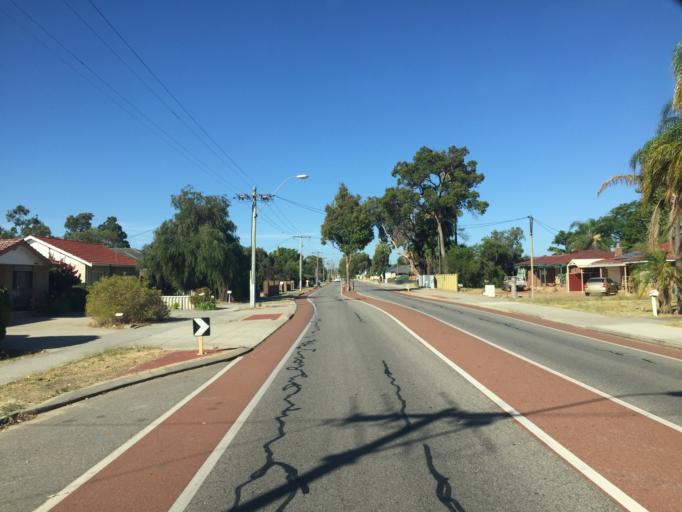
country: AU
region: Western Australia
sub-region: Canning
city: East Cannington
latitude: -32.0161
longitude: 115.9623
